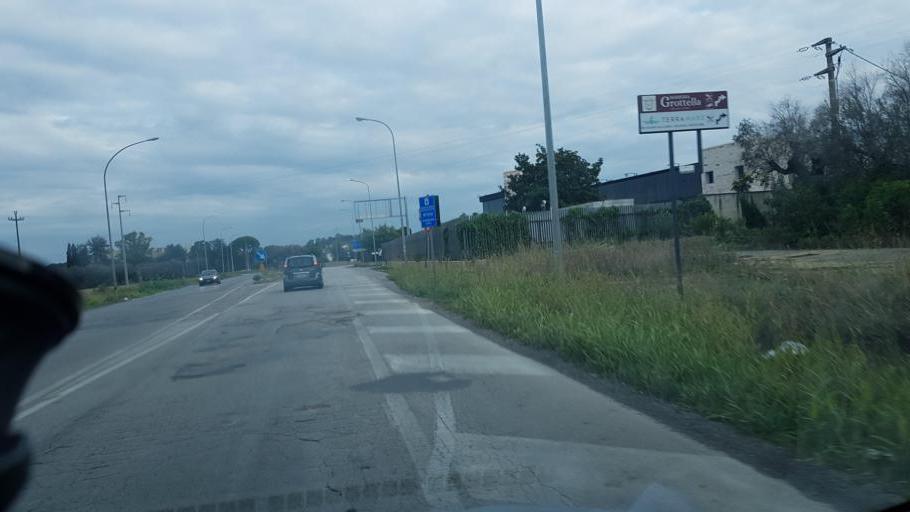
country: IT
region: Apulia
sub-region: Provincia di Brindisi
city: Oria
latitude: 40.5068
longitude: 17.6286
